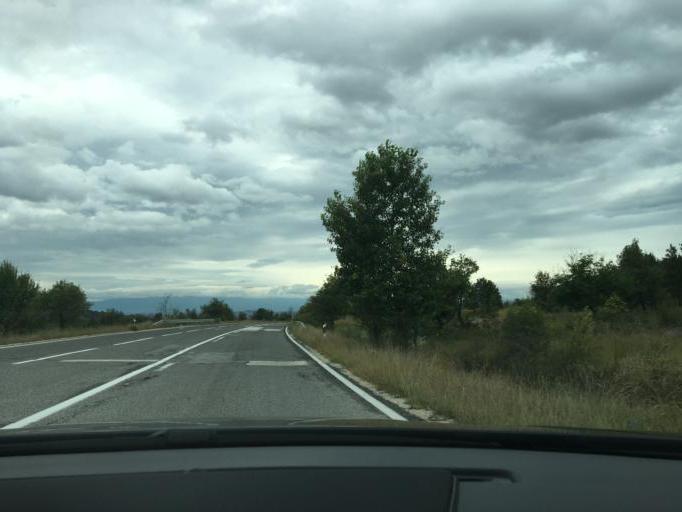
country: MK
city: Klechovce
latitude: 42.1493
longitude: 21.9680
